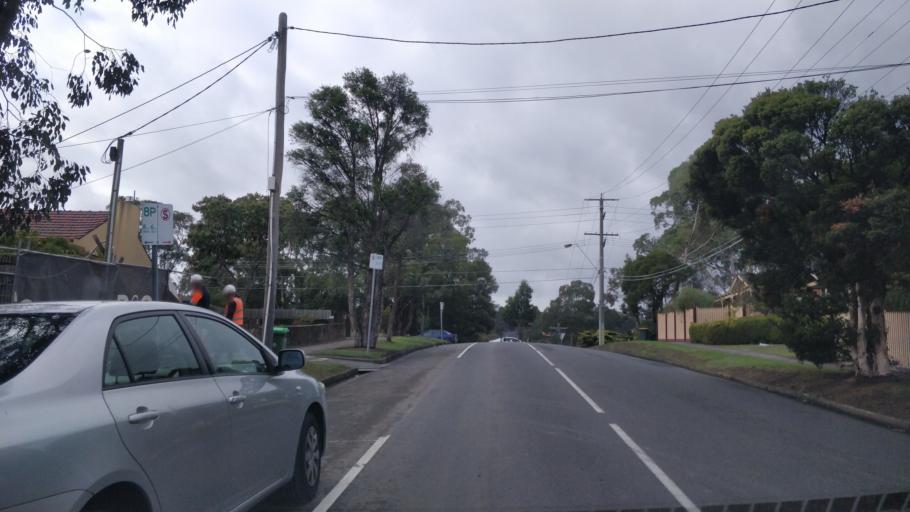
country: AU
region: Victoria
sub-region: Nillumbik
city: Eltham North
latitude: -37.7147
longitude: 145.1511
